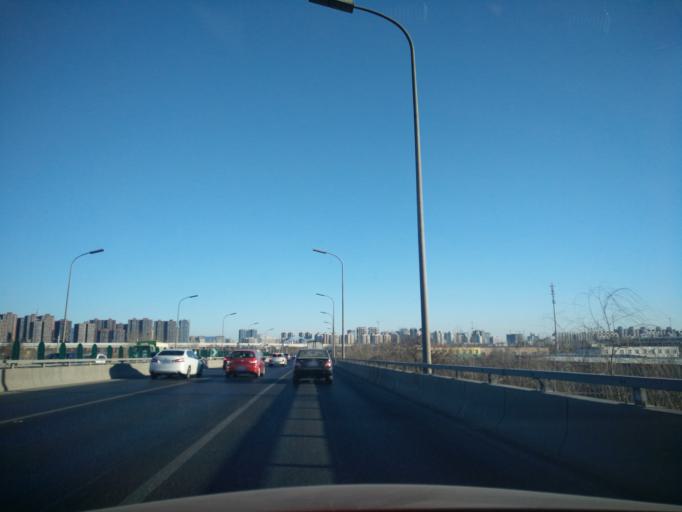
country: CN
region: Beijing
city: Lugu
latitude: 39.8813
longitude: 116.2026
